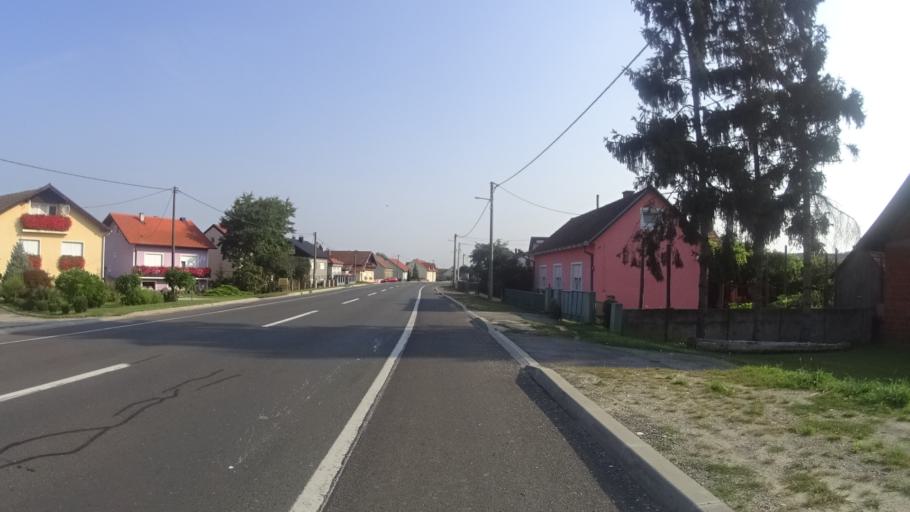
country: HR
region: Medimurska
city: Nedelisce
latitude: 46.3500
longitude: 16.3628
